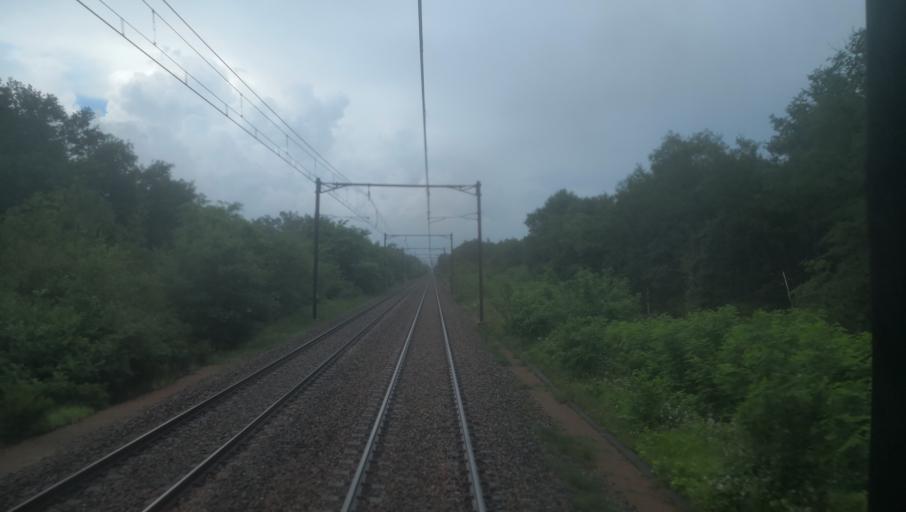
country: FR
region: Centre
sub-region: Departement du Loiret
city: La Ferte-Saint-Aubin
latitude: 47.7758
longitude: 1.9392
